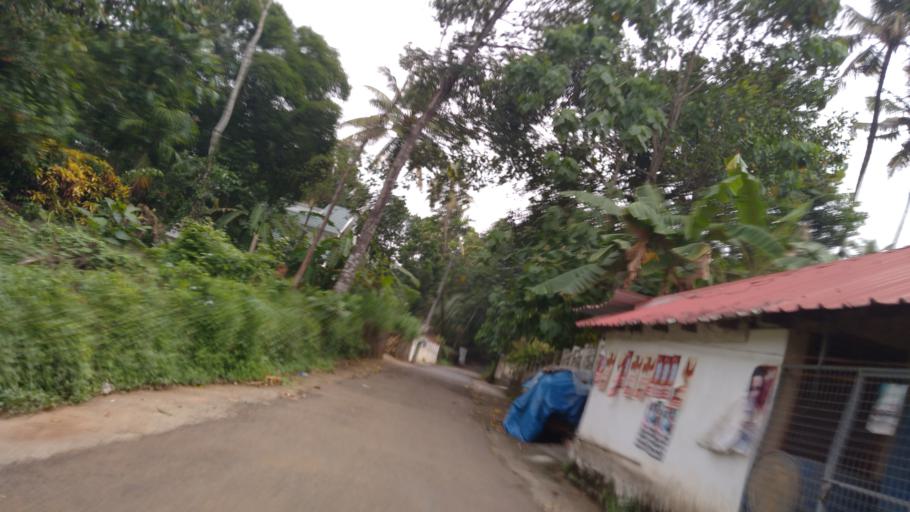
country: IN
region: Kerala
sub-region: Ernakulam
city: Kotamangalam
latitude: 10.1196
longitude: 76.5778
